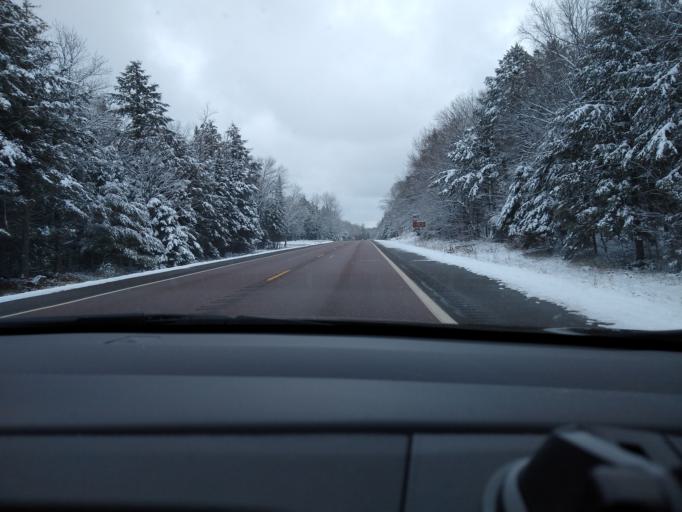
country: US
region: Wisconsin
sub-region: Vilas County
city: Eagle River
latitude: 46.2482
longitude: -89.1051
